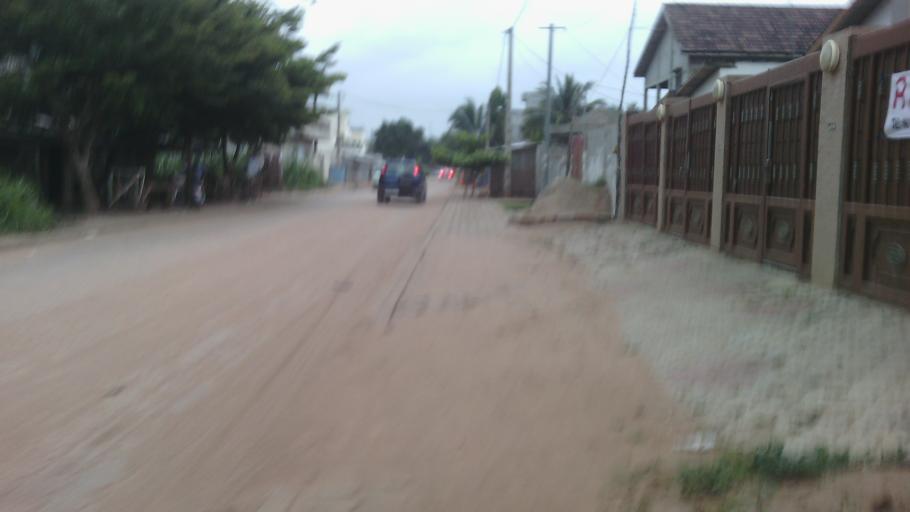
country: BJ
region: Atlantique
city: Abomey-Calavi
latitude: 6.4780
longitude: 2.3505
